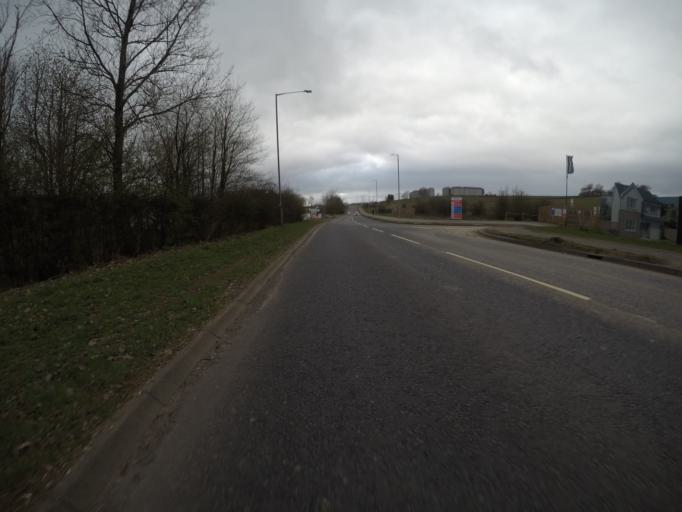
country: GB
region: Scotland
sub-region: East Ayrshire
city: Crosshouse
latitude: 55.6115
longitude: -4.5268
